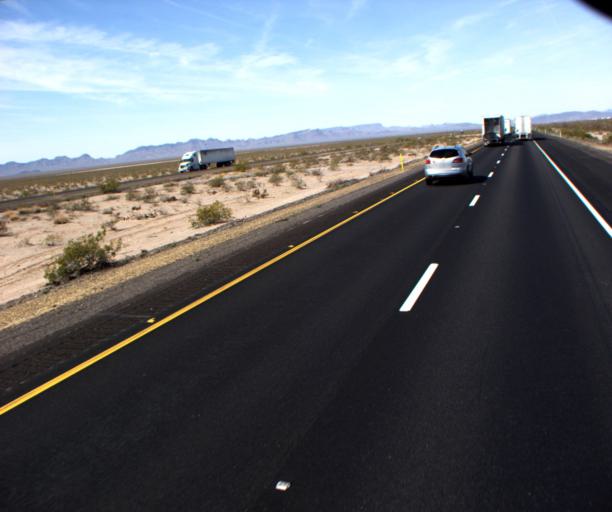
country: US
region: Arizona
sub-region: La Paz County
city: Salome
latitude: 33.6187
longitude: -113.6827
